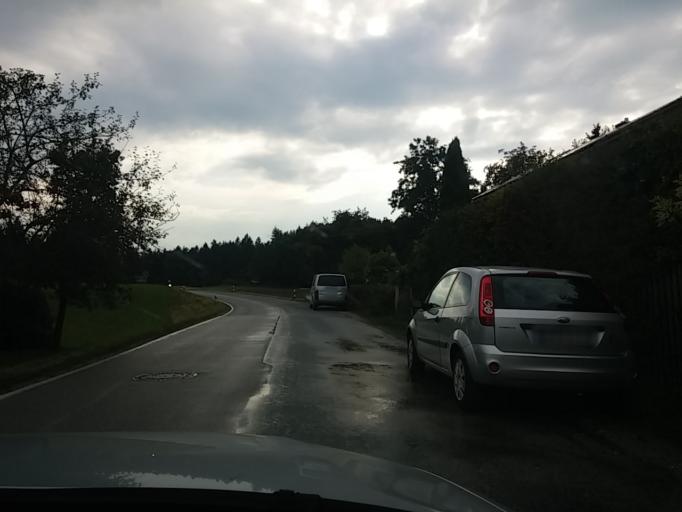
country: DE
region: Bavaria
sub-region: Upper Bavaria
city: Reichertshausen
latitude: 47.9418
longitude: 11.5759
